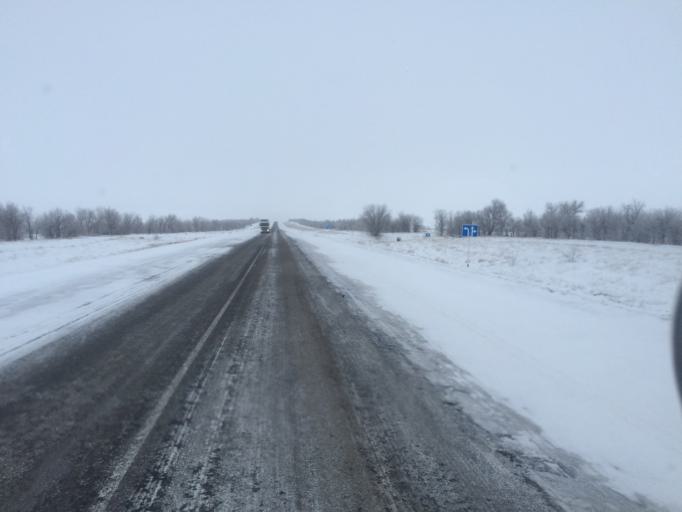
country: KZ
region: Aqtoebe
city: Martuk
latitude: 50.1884
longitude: 55.8428
